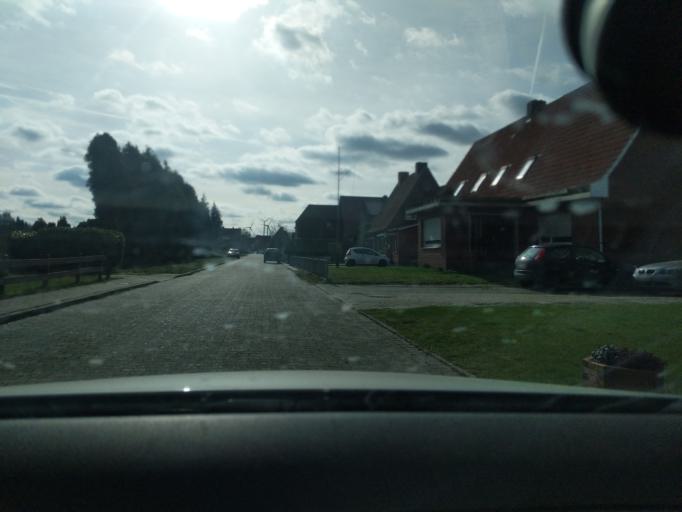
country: DE
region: Lower Saxony
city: Drochtersen
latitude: 53.7130
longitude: 9.3846
